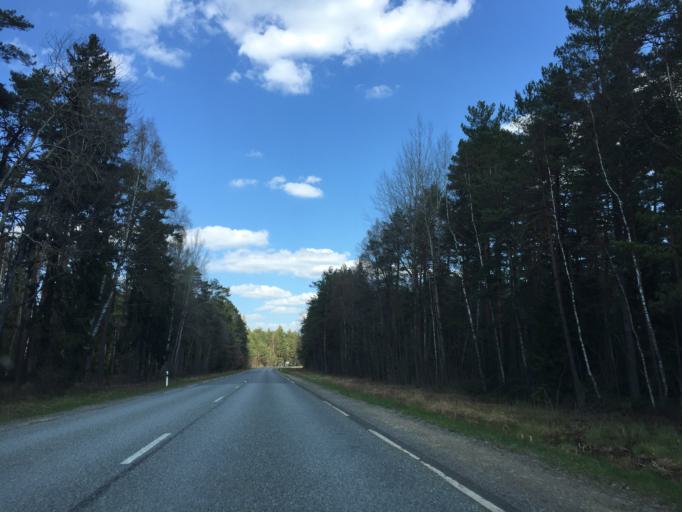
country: LV
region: Saulkrastu
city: Saulkrasti
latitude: 57.2119
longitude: 24.3822
